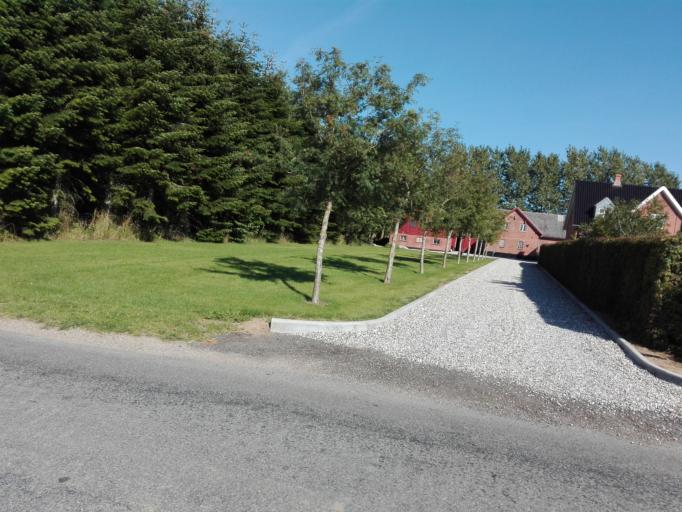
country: DK
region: Central Jutland
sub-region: Odder Kommune
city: Odder
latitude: 55.9535
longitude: 10.1102
